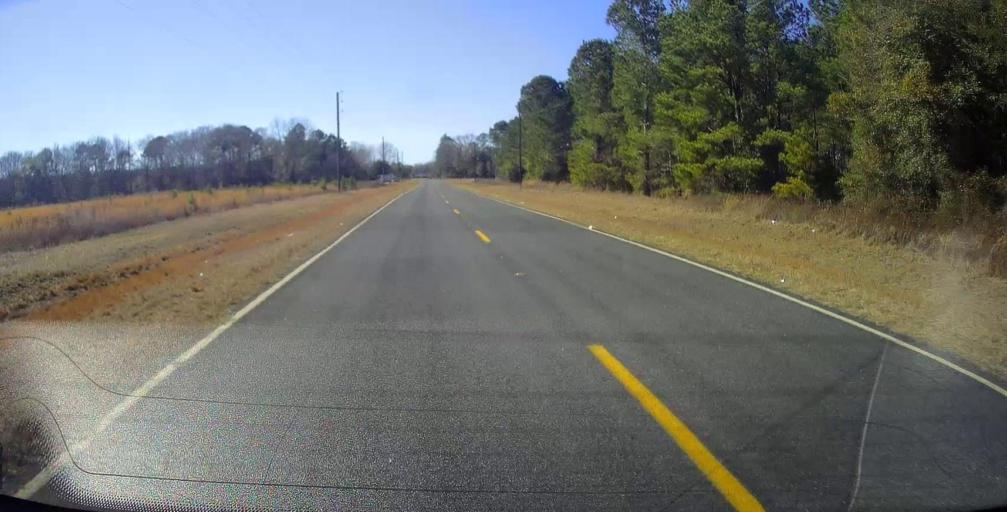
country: US
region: Georgia
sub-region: Macon County
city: Montezuma
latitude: 32.2800
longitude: -84.0214
